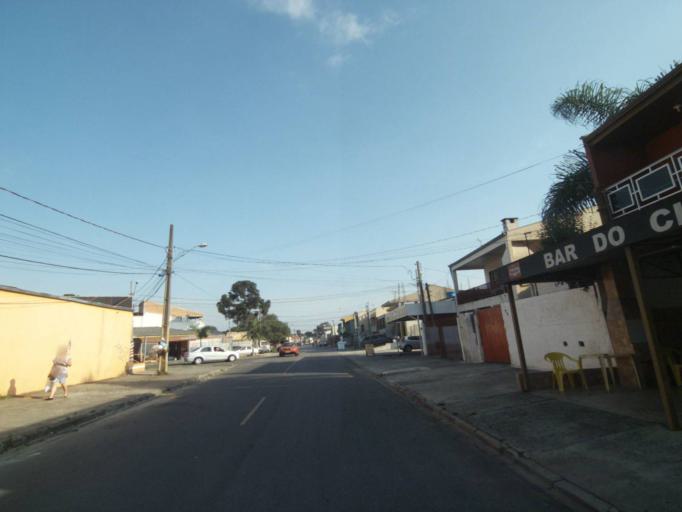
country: BR
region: Parana
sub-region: Curitiba
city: Curitiba
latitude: -25.4865
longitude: -49.3362
